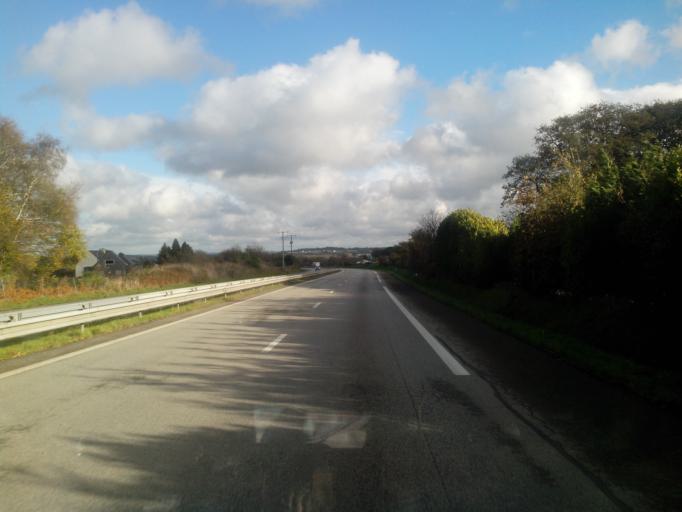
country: FR
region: Brittany
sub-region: Departement du Morbihan
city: Quistinic
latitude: 47.8596
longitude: -3.1003
